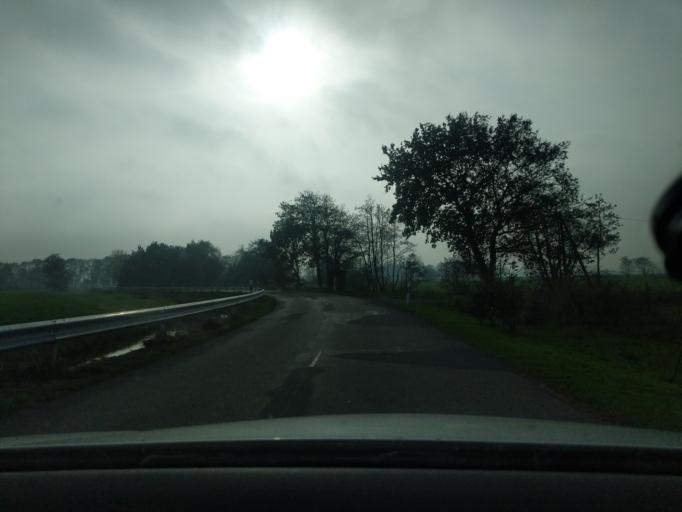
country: DE
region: Lower Saxony
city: Wanna
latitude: 53.7798
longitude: 8.7442
